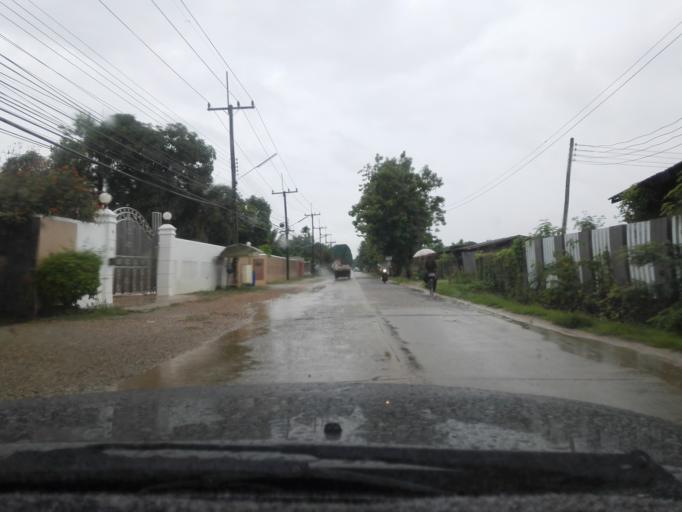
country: TH
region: Tak
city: Mae Sot
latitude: 16.6929
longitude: 98.5749
